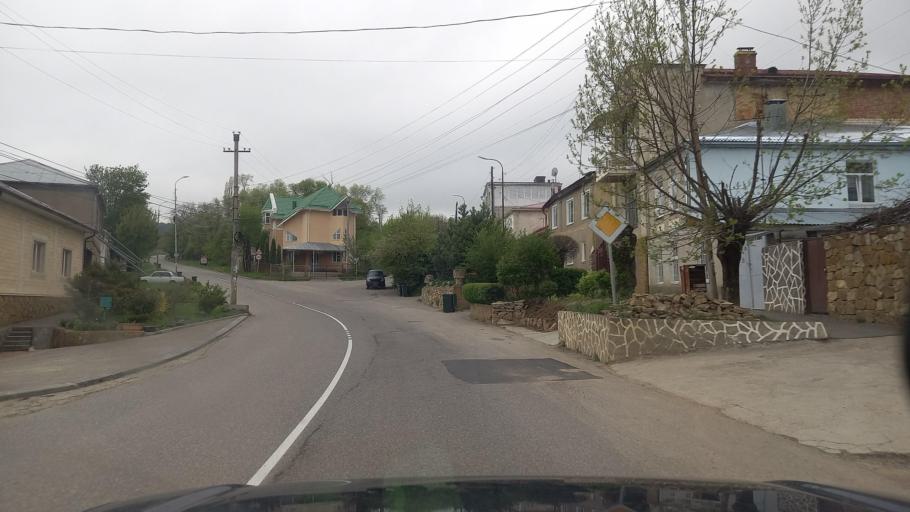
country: RU
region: Stavropol'skiy
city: Kislovodsk
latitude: 43.8925
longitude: 42.7059
